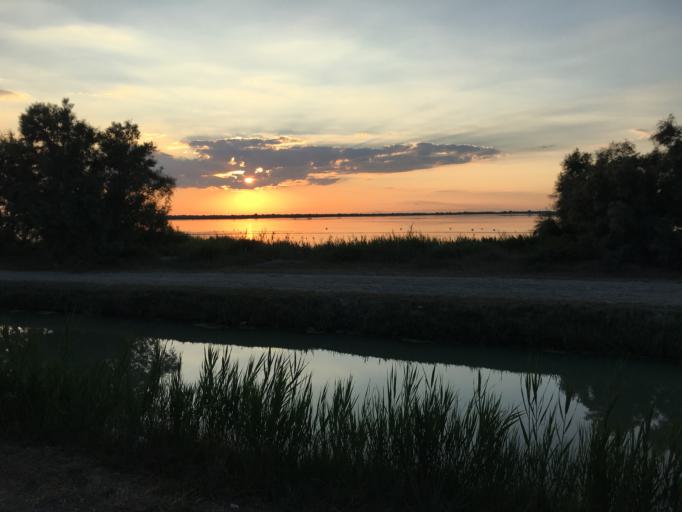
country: FR
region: Provence-Alpes-Cote d'Azur
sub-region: Departement des Bouches-du-Rhone
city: Saintes-Maries-de-la-Mer
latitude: 43.4506
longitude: 4.4233
